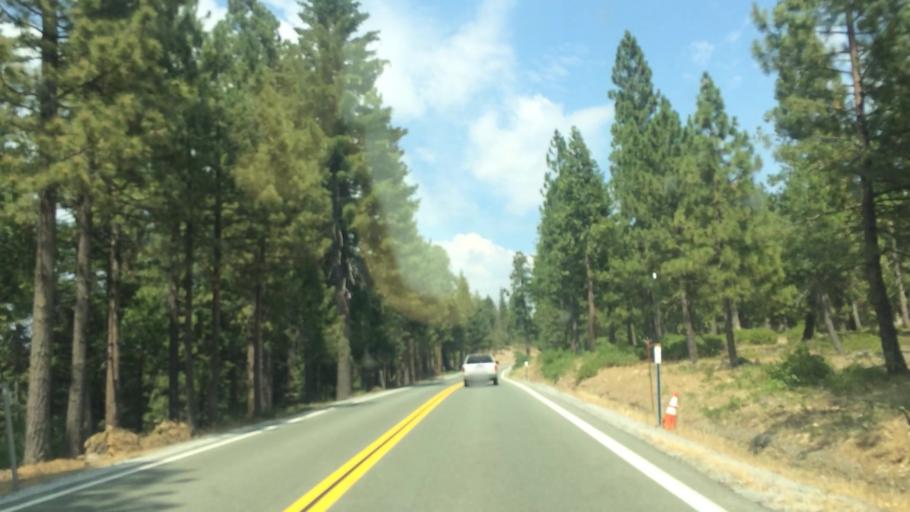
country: US
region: California
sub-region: Amador County
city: Pioneer
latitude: 38.5347
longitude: -120.4070
